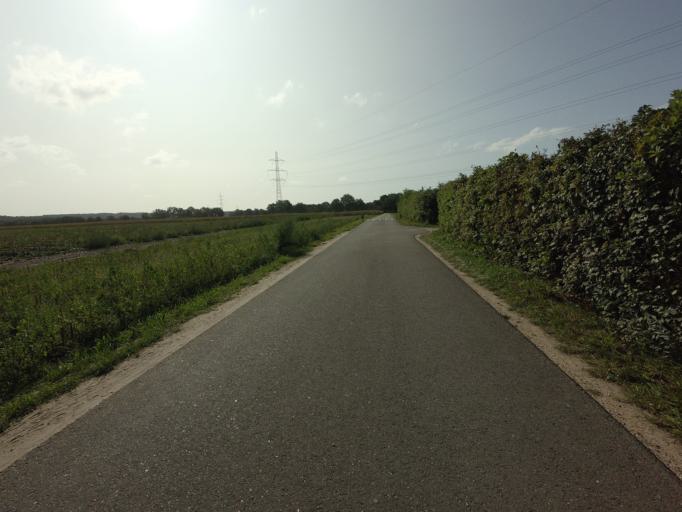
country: NL
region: Limburg
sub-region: Gemeente Roerdalen
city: Herkenbosch
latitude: 51.1944
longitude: 6.0617
